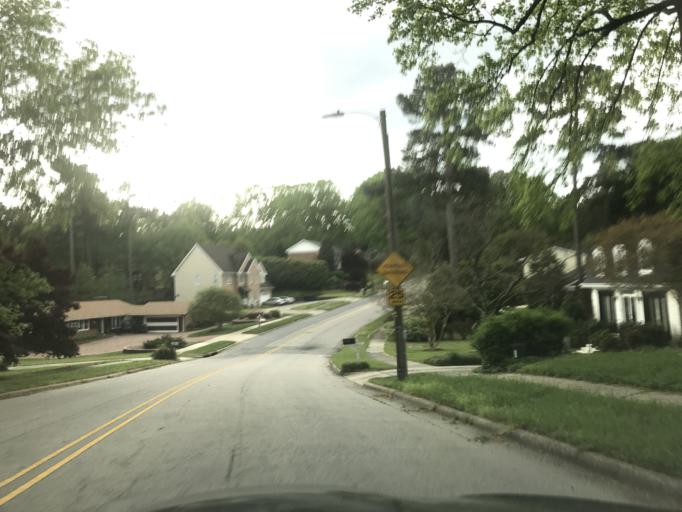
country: US
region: North Carolina
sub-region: Wake County
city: West Raleigh
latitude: 35.7841
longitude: -78.7064
